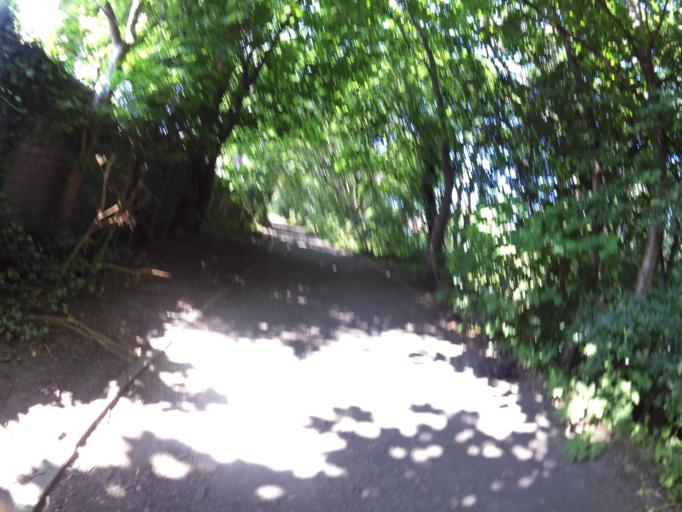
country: GB
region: Scotland
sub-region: Edinburgh
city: Colinton
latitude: 55.9295
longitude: -3.2534
